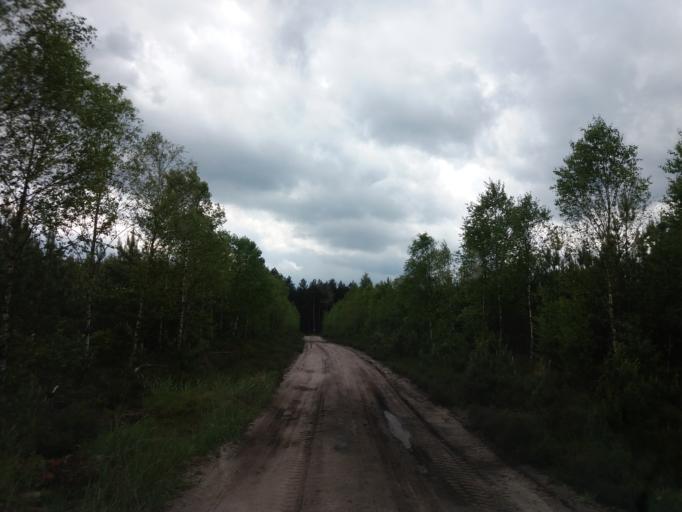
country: PL
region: West Pomeranian Voivodeship
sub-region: Powiat choszczenski
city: Drawno
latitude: 53.1552
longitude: 15.7576
